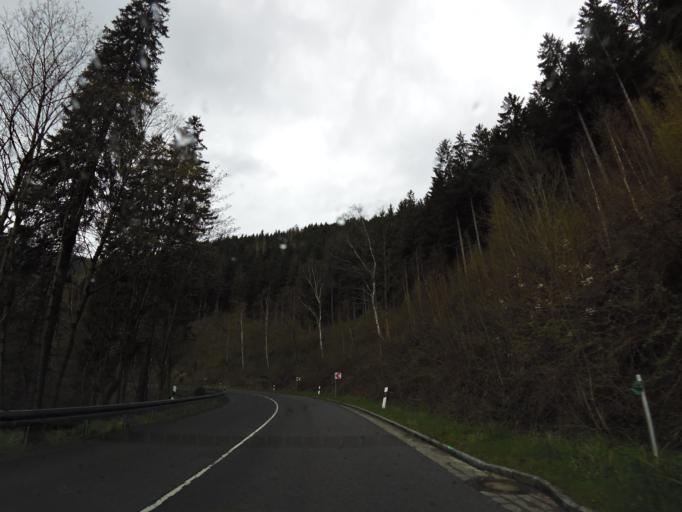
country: DE
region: Lower Saxony
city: Schulenberg im Oberharz
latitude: 51.8671
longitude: 10.4750
